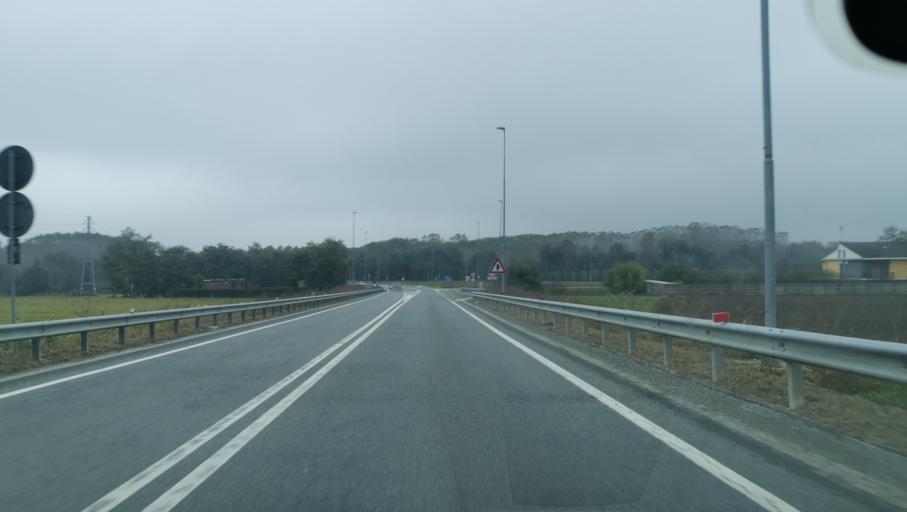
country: IT
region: Piedmont
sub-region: Provincia di Torino
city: Rondissone
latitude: 45.2538
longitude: 7.9654
